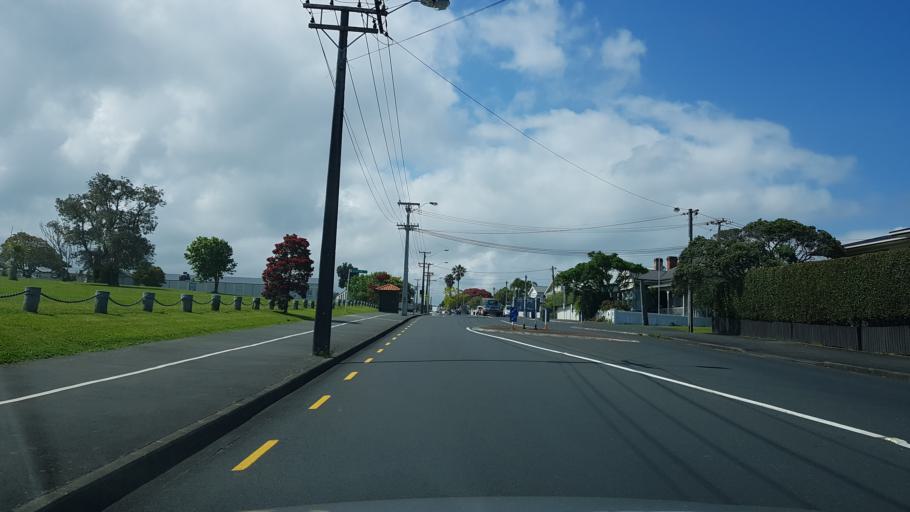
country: NZ
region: Auckland
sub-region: Auckland
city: North Shore
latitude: -36.8141
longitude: 174.8031
